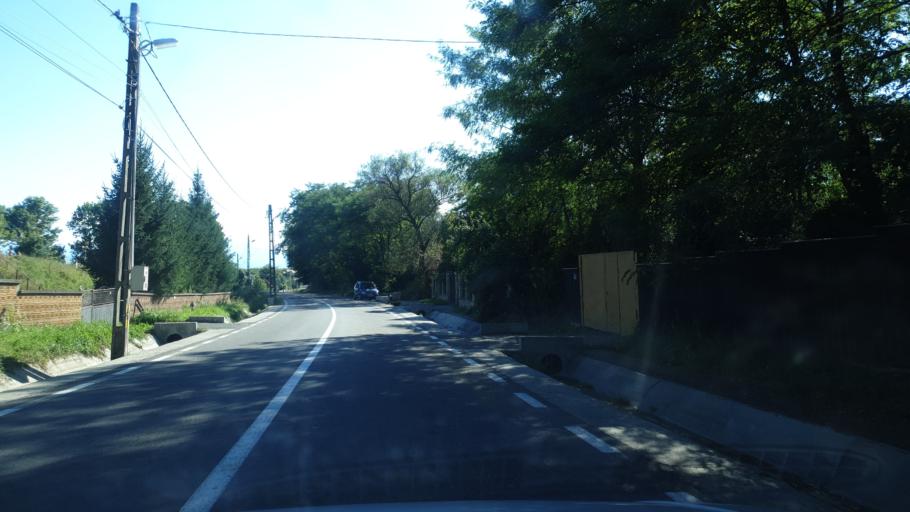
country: RO
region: Covasna
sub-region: Comuna Ilieni
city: Ilieni
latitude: 45.7771
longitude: 25.7526
